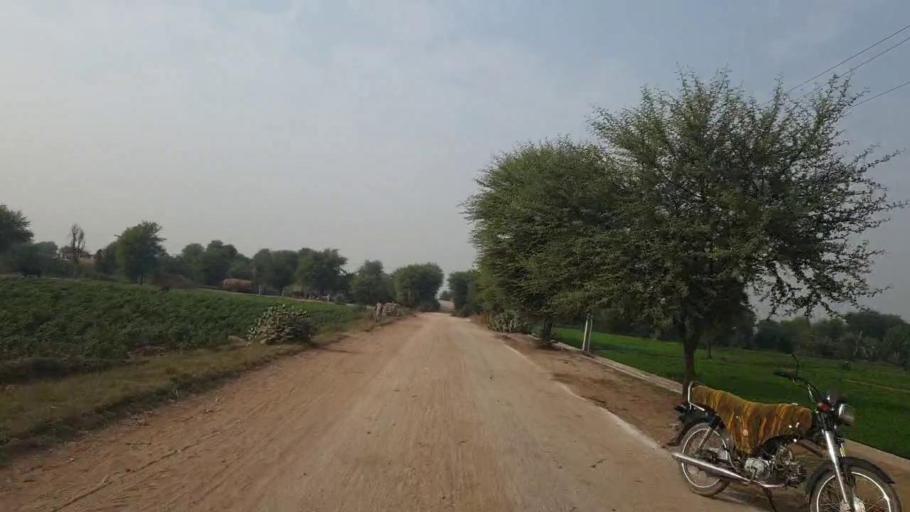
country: PK
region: Sindh
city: Sann
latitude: 26.0682
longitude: 68.1153
